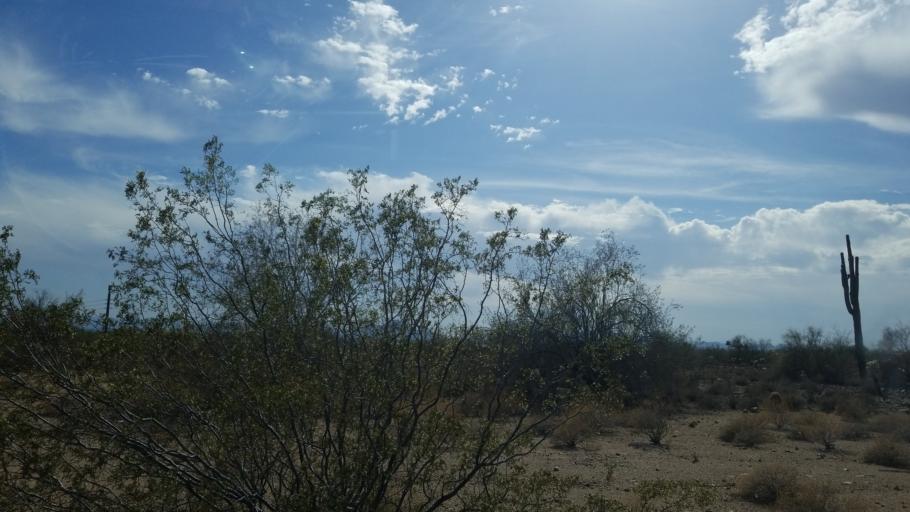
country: US
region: Arizona
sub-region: Maricopa County
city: Fountain Hills
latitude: 33.5843
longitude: -111.7963
